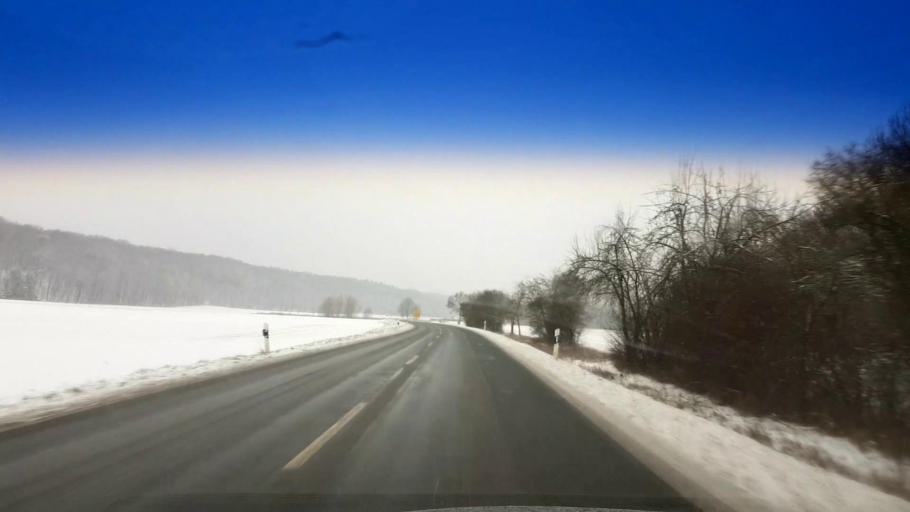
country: DE
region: Bavaria
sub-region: Upper Franconia
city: Memmelsdorf
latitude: 49.9438
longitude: 10.9833
